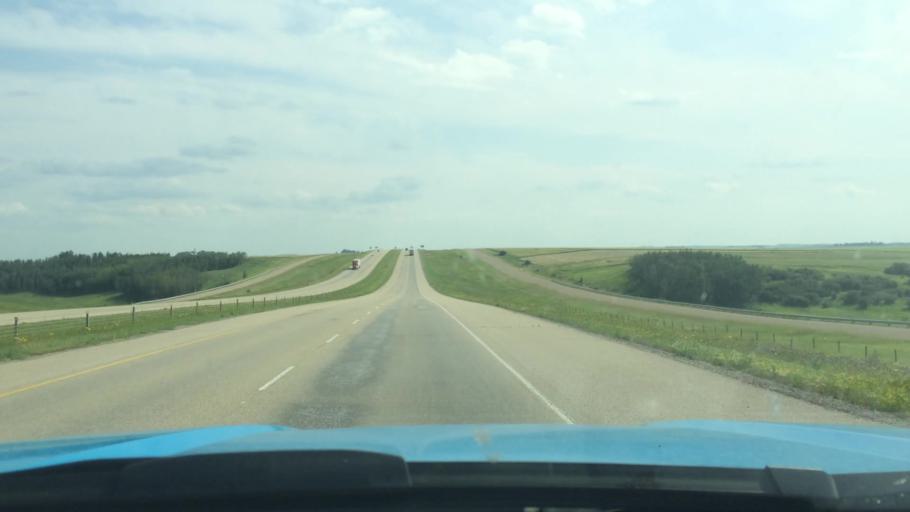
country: CA
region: Alberta
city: Carstairs
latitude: 51.5804
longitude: -114.0253
